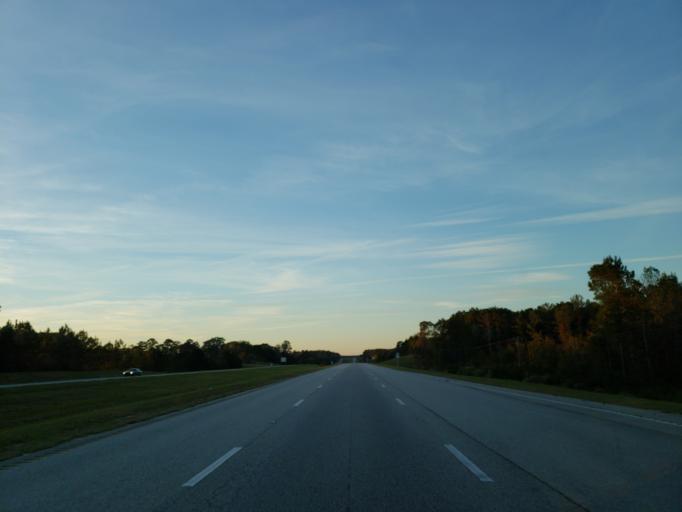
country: US
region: Mississippi
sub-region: Wayne County
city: Belmont
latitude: 31.4613
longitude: -88.4693
